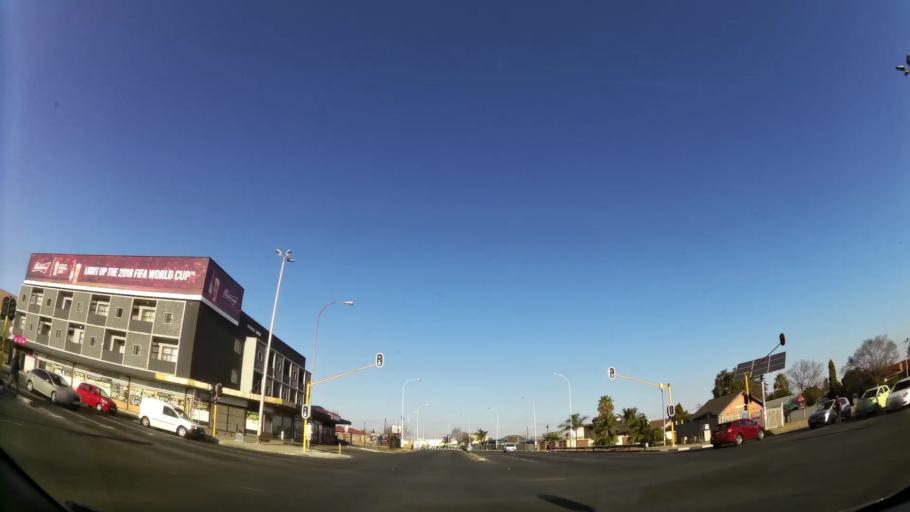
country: ZA
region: Gauteng
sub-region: City of Johannesburg Metropolitan Municipality
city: Roodepoort
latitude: -26.1688
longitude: 27.9310
